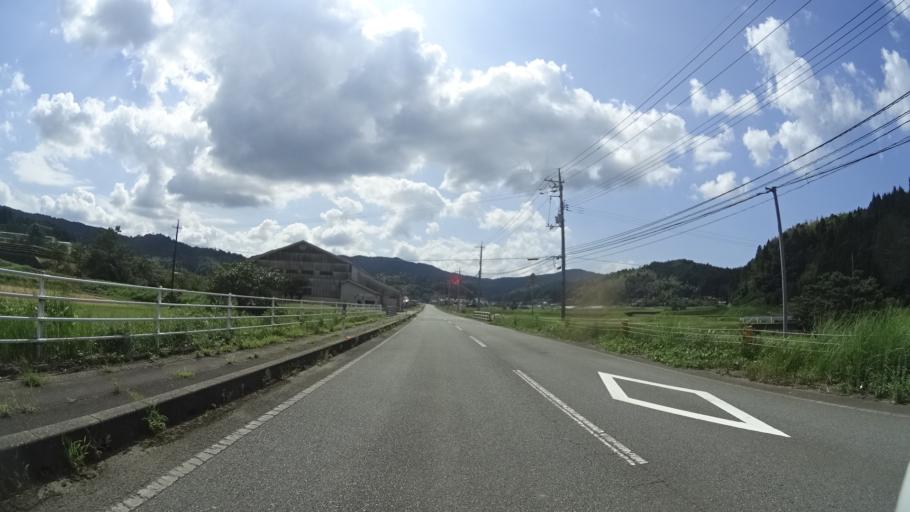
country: JP
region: Yamaguchi
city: Hagi
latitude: 34.4383
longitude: 131.4863
